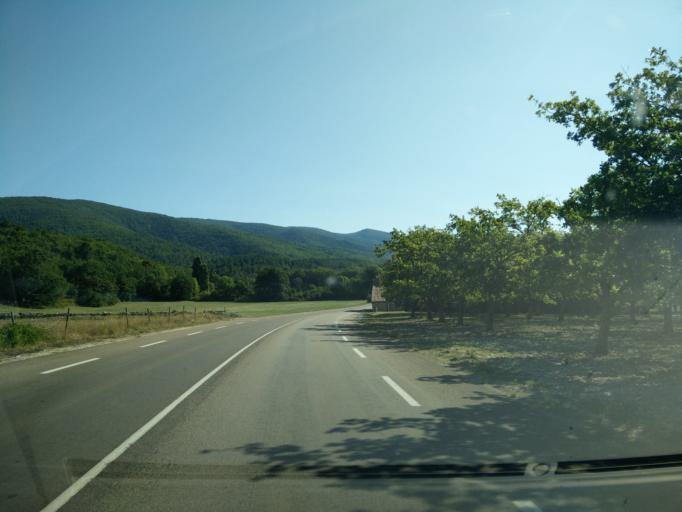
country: FR
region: Rhone-Alpes
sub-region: Departement de la Drome
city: La Begude-de-Mazenc
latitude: 44.5301
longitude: 4.9903
